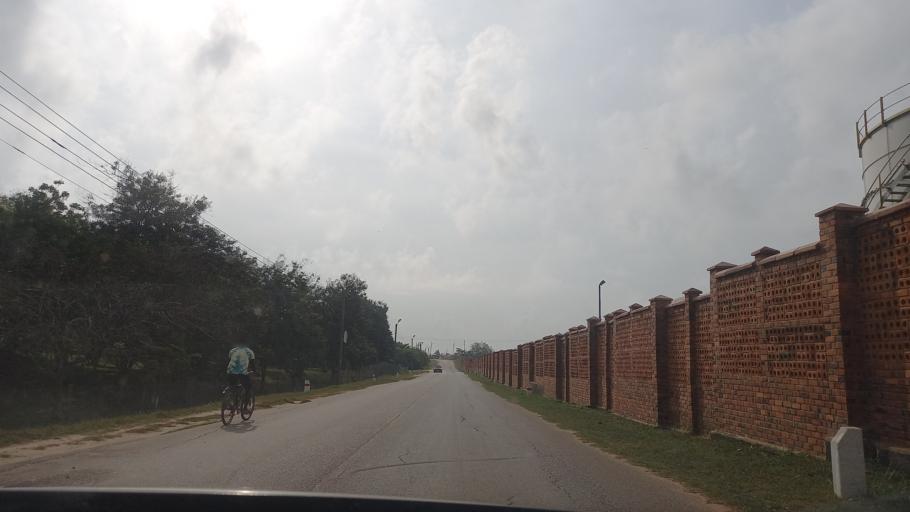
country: GH
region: Western
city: Shama Junction
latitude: 4.9760
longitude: -1.6581
